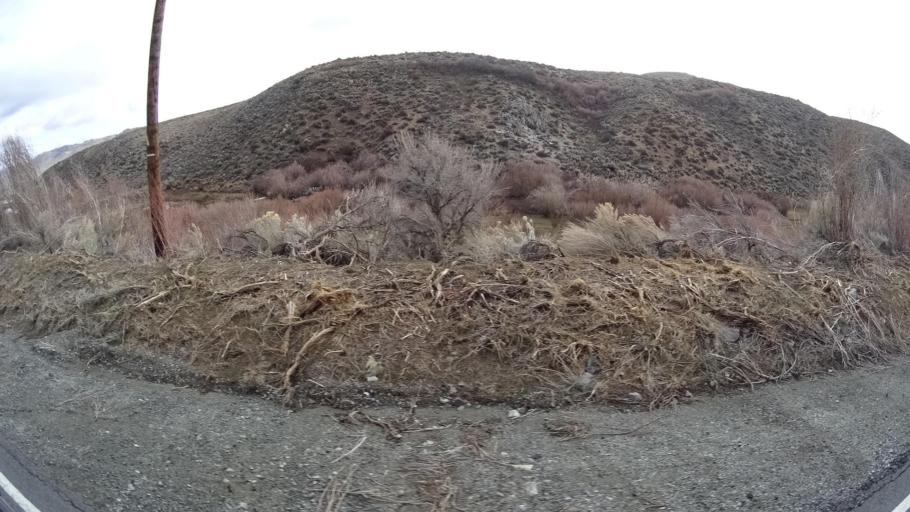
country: US
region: Nevada
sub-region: Washoe County
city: Cold Springs
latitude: 39.8297
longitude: -119.9388
